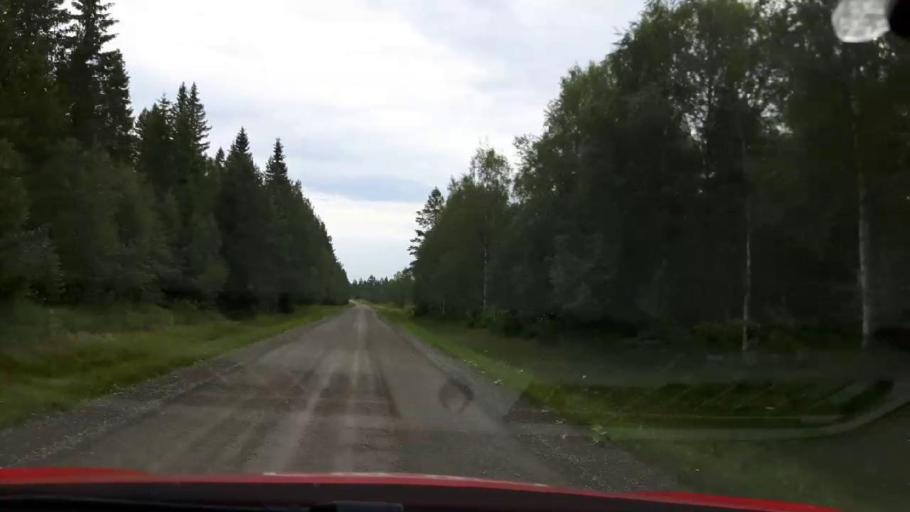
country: SE
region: Jaemtland
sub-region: Stroemsunds Kommun
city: Stroemsund
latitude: 63.7160
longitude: 15.4928
